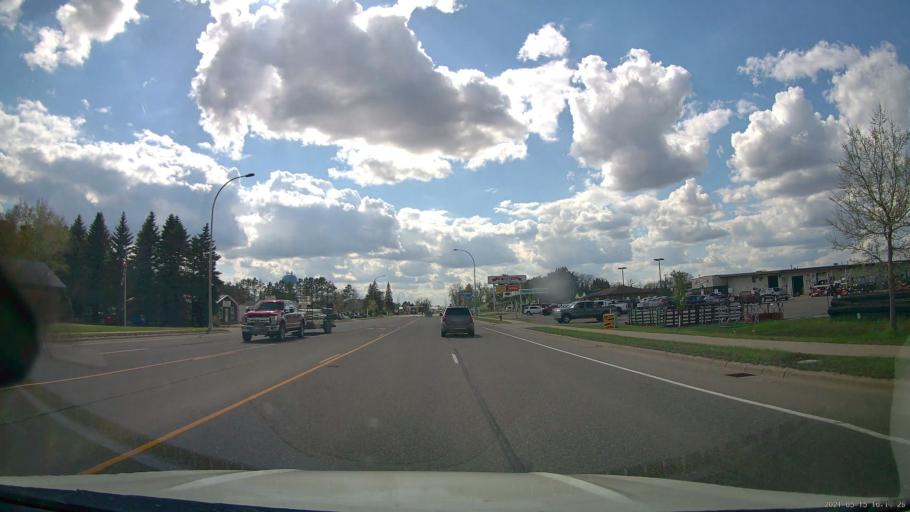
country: US
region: Minnesota
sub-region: Hubbard County
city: Park Rapids
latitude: 46.9220
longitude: -95.0325
